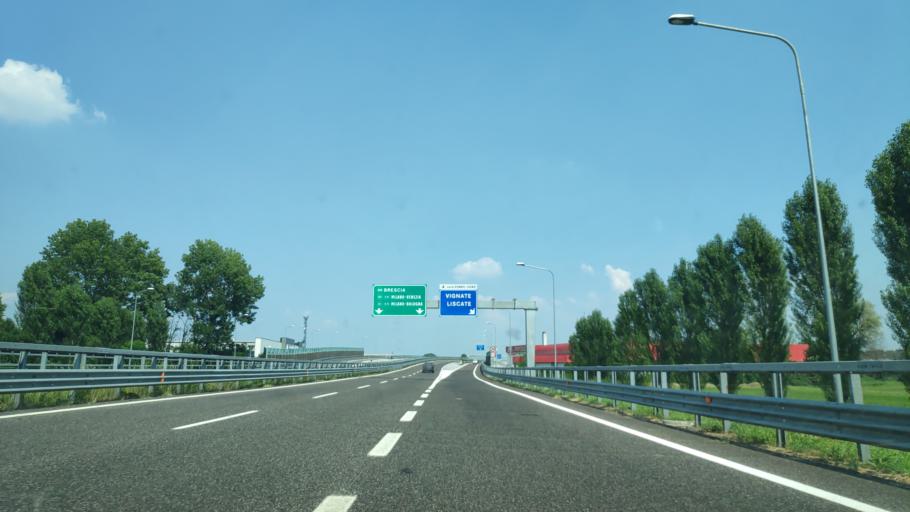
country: IT
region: Lombardy
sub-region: Citta metropolitana di Milano
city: Vignate
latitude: 45.4838
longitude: 9.3728
